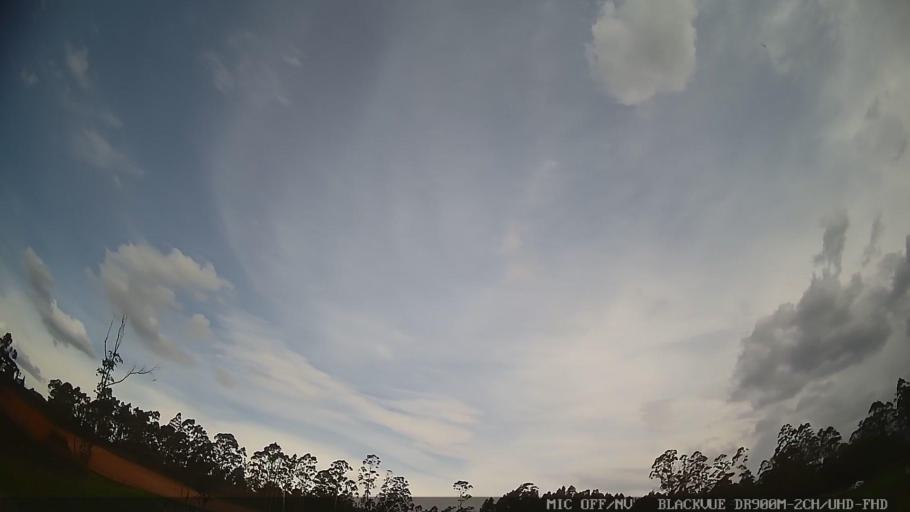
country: BR
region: Sao Paulo
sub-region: Amparo
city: Amparo
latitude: -22.7845
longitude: -46.7532
